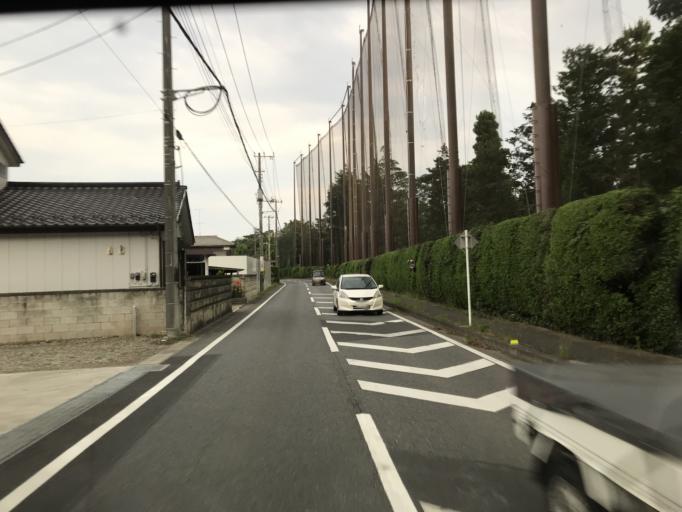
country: JP
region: Chiba
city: Noda
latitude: 35.9597
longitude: 139.8902
